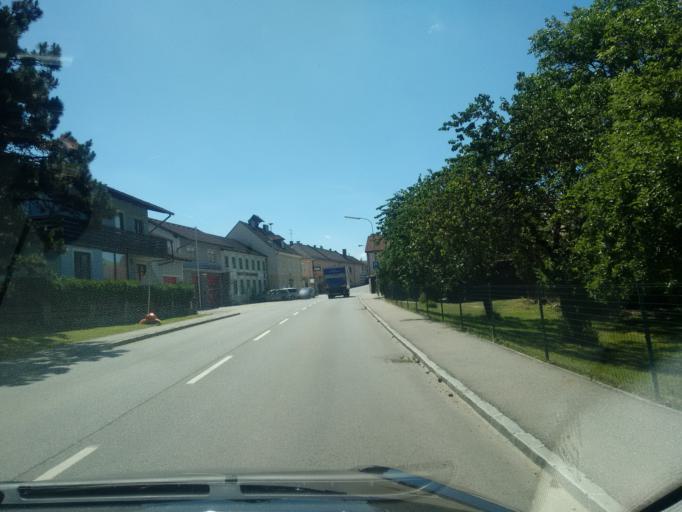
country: AT
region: Lower Austria
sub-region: Politischer Bezirk Sankt Polten
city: Haunoldstein
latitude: 48.1933
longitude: 15.4593
